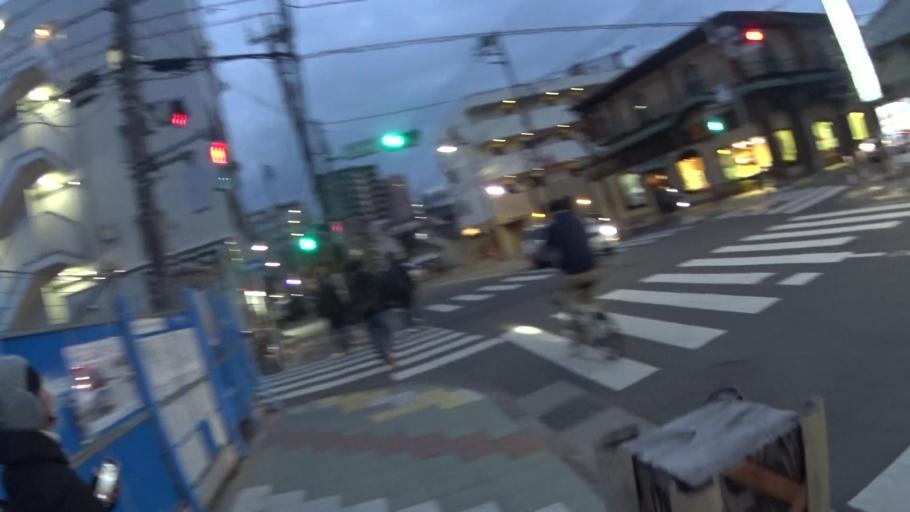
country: JP
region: Kanagawa
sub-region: Kawasaki-shi
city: Kawasaki
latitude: 35.5752
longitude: 139.7048
